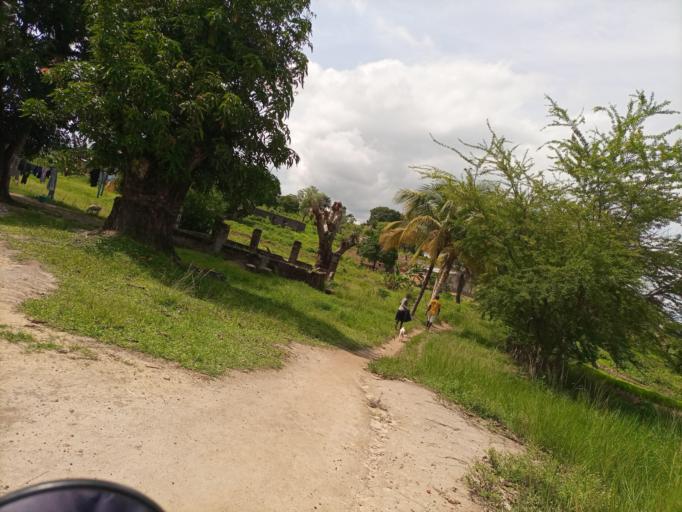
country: SL
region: Southern Province
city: Bo
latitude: 7.9714
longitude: -11.7597
